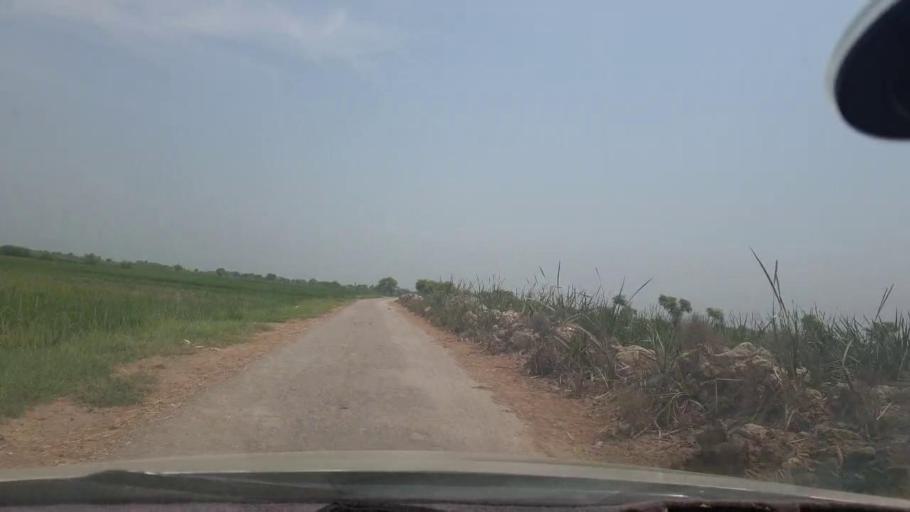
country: PK
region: Sindh
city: Jacobabad
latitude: 28.1800
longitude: 68.3793
